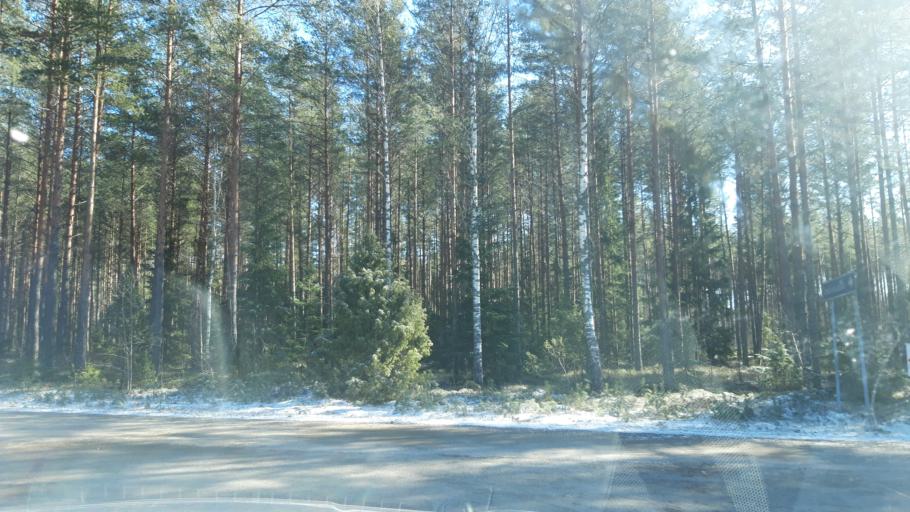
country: LV
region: Strenci
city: Strenci
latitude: 57.5757
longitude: 25.7095
